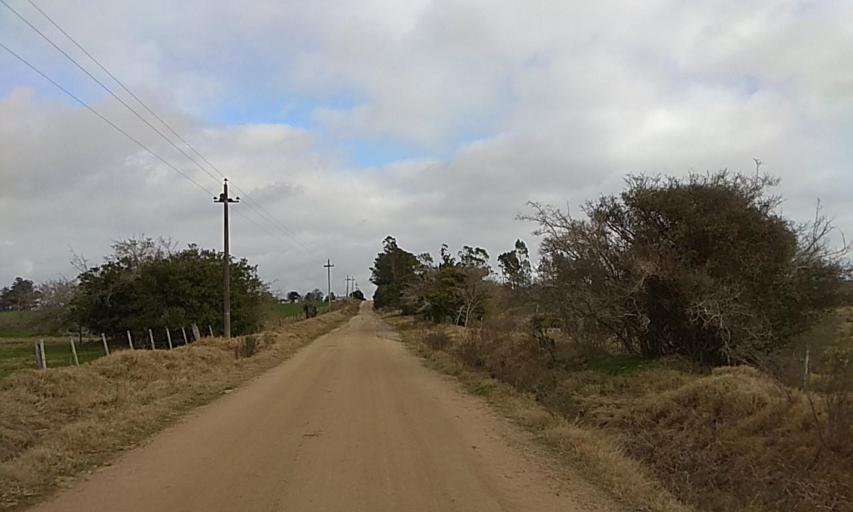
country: UY
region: Florida
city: Florida
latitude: -34.0623
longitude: -56.1999
